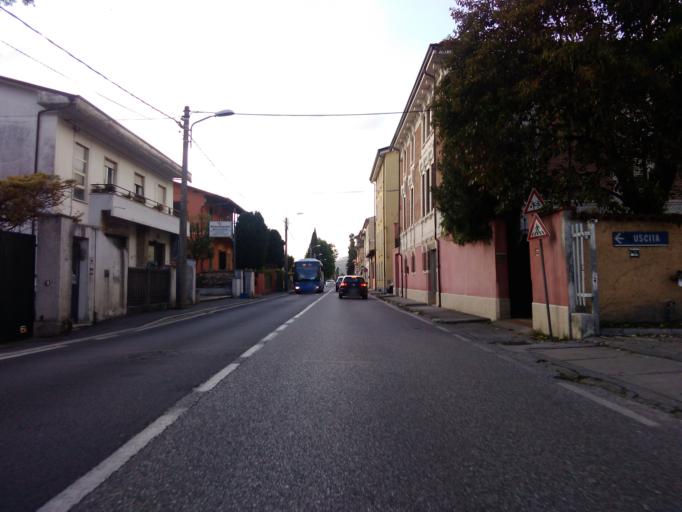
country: IT
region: Tuscany
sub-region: Provincia di Lucca
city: Pietrasanta
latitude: 43.9622
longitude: 10.2257
